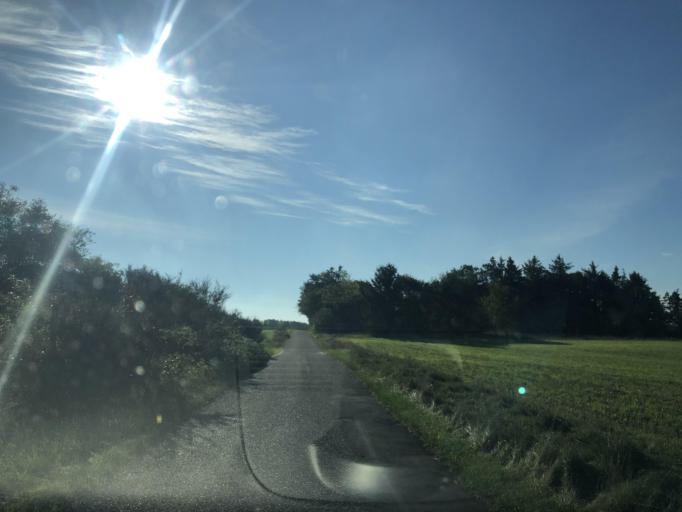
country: DK
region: Central Jutland
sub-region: Holstebro Kommune
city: Holstebro
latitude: 56.3096
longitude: 8.5048
